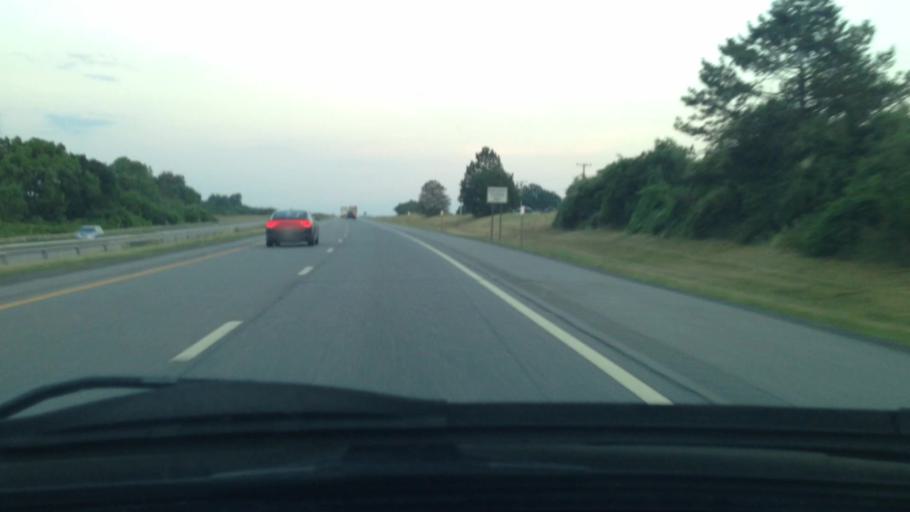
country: US
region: New York
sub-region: Montgomery County
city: Fort Plain
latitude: 42.9651
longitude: -74.6432
